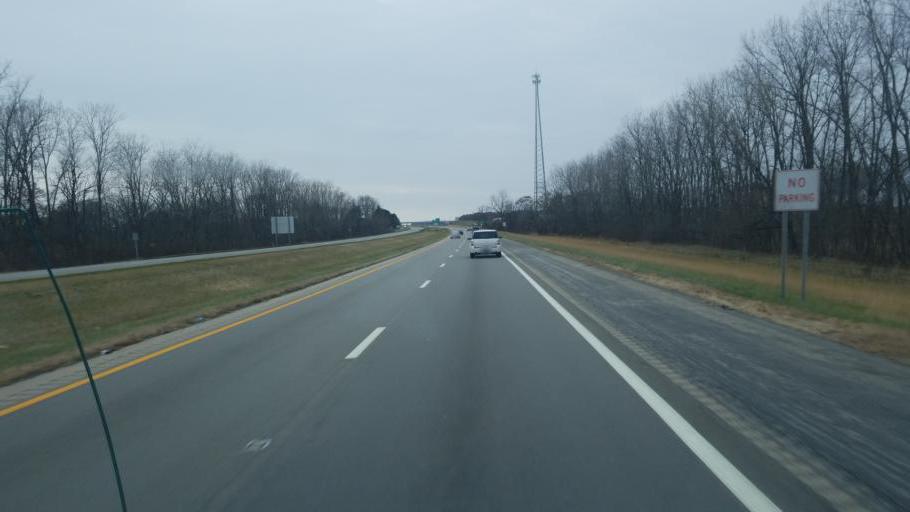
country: US
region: Ohio
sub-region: Auglaize County
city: Saint Marys
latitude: 40.5577
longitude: -84.3893
